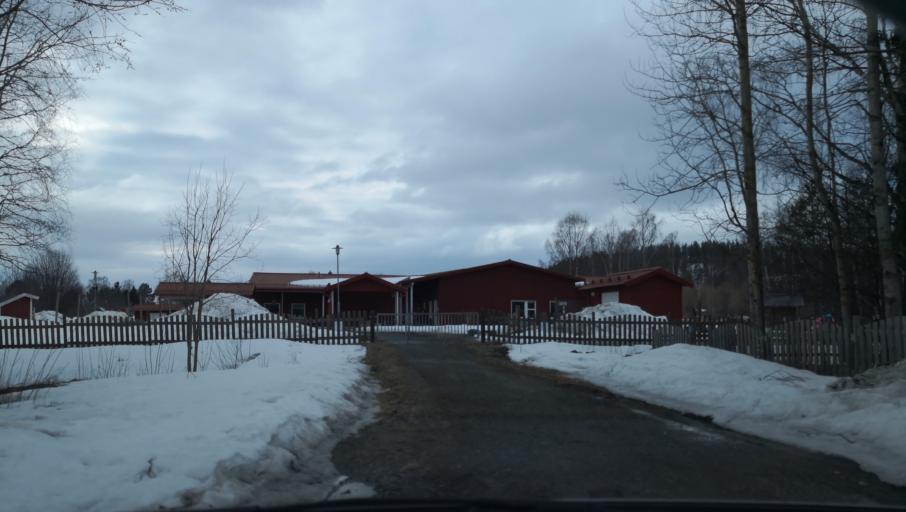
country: SE
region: Vaesterbotten
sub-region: Vannas Kommun
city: Vannasby
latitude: 63.9182
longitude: 19.8126
